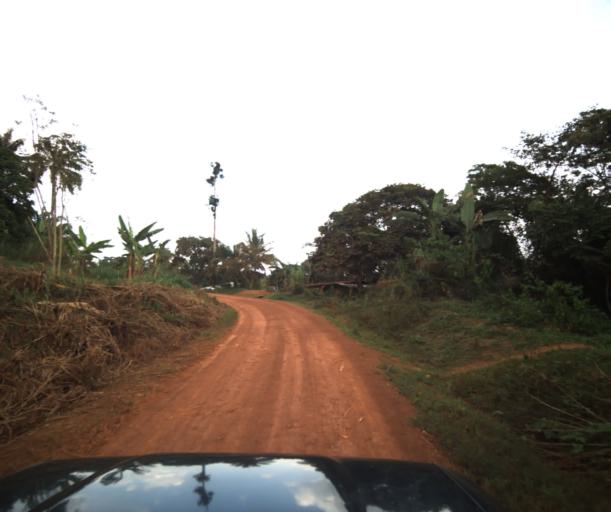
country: CM
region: Centre
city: Akono
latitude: 3.6035
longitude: 11.1884
